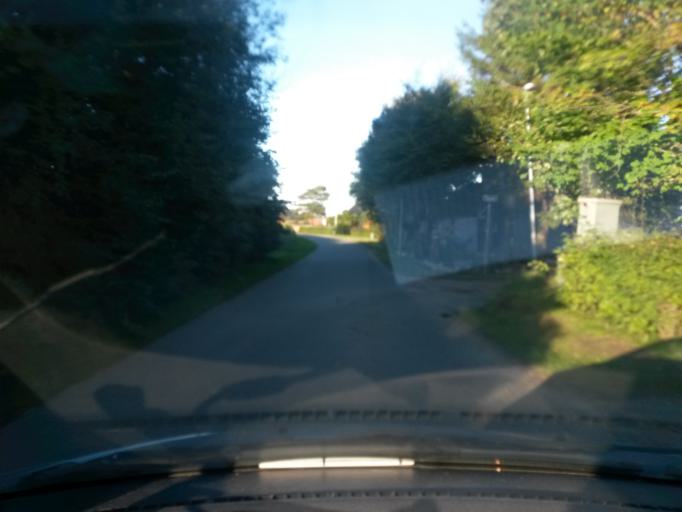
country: DK
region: Central Jutland
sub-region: Silkeborg Kommune
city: Kjellerup
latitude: 56.3297
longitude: 9.4451
